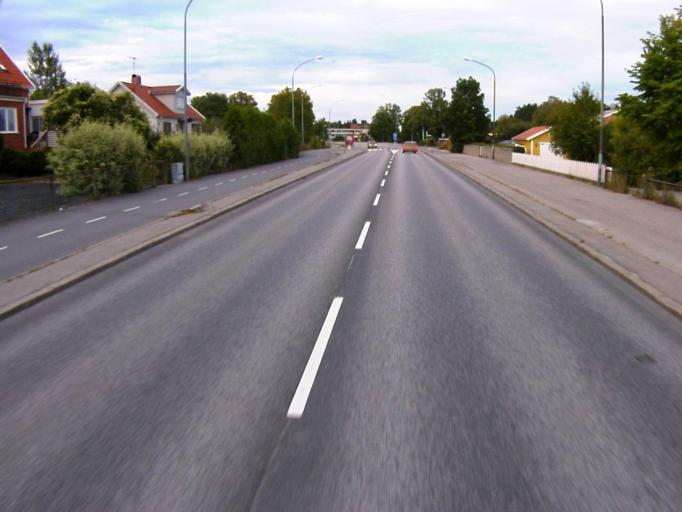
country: SE
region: Soedermanland
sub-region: Eskilstuna Kommun
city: Torshalla
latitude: 59.3977
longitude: 16.4873
